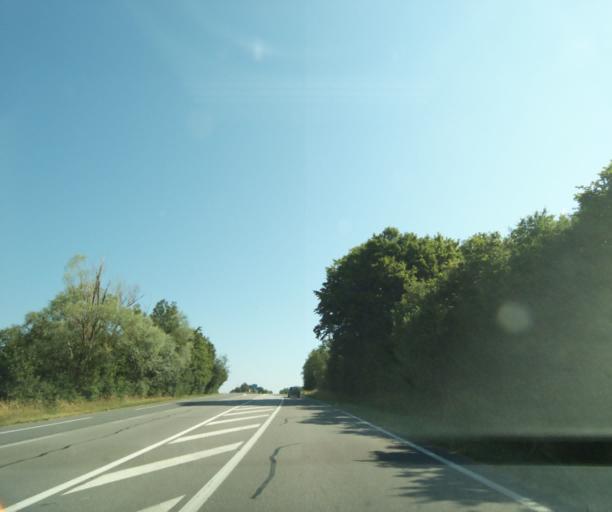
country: FR
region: Lorraine
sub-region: Departement de Meurthe-et-Moselle
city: Ecrouves
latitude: 48.6468
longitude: 5.8682
